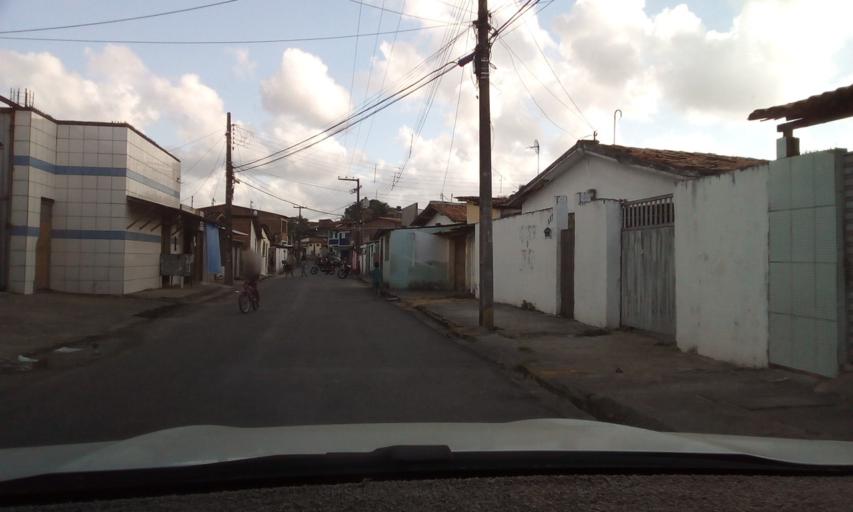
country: BR
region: Paraiba
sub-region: Joao Pessoa
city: Joao Pessoa
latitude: -7.0935
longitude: -34.8606
